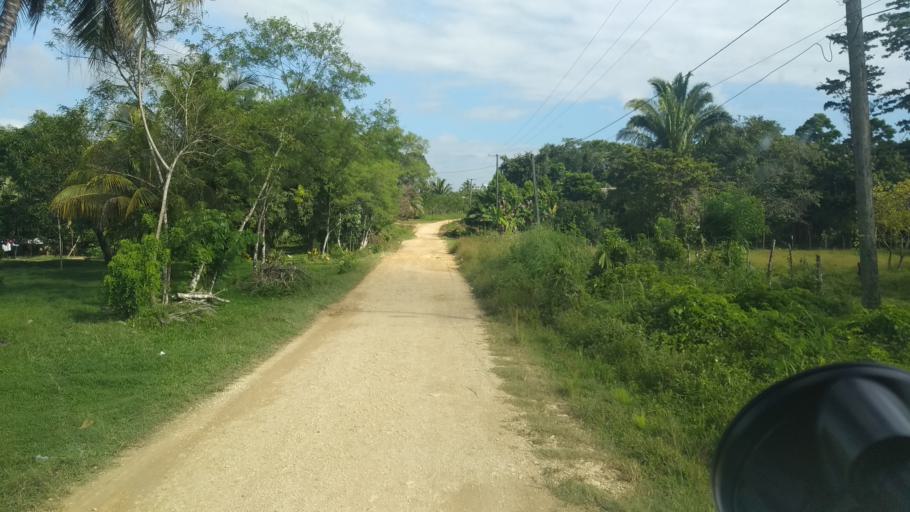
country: BZ
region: Toledo
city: Punta Gorda
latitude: 16.2086
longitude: -88.9134
